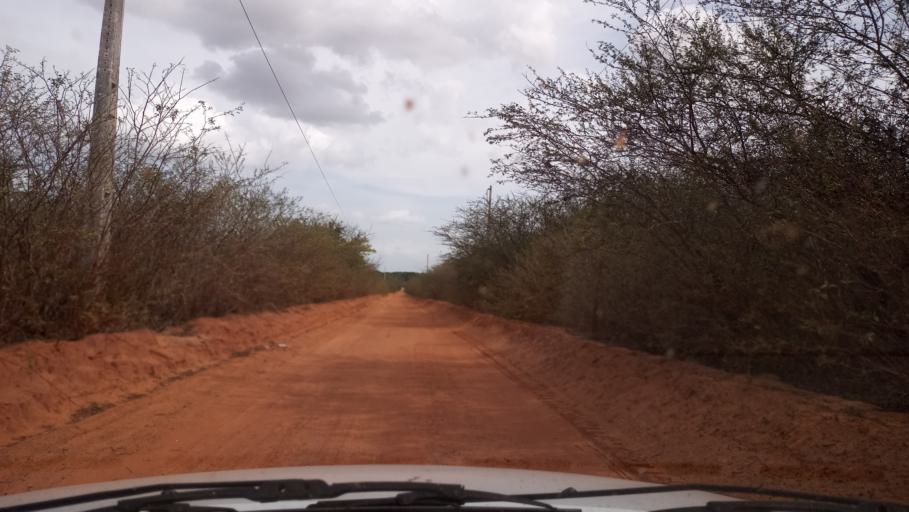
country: BR
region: Rio Grande do Norte
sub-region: Joao Camara
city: Joao Camara
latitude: -5.4997
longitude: -35.8258
